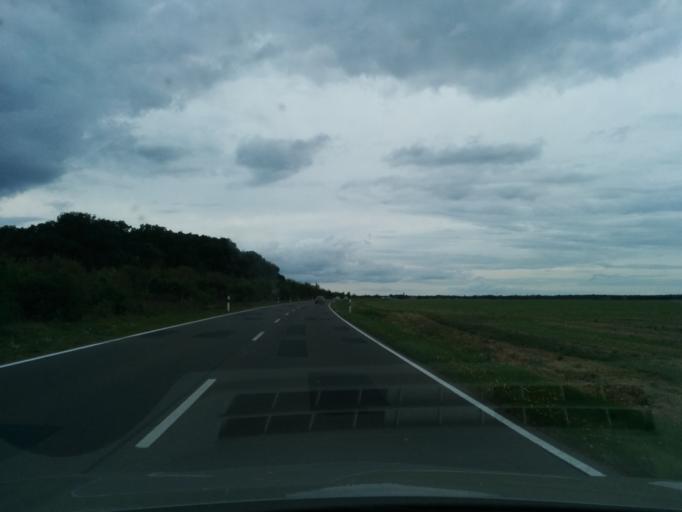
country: DE
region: Mecklenburg-Vorpommern
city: Gross Kiesow
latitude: 53.9371
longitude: 13.4358
